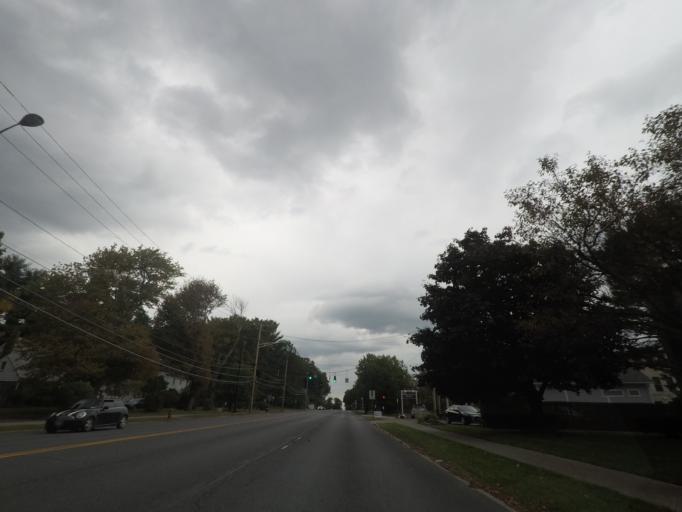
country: US
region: New York
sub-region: Albany County
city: Roessleville
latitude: 42.6744
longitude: -73.8170
